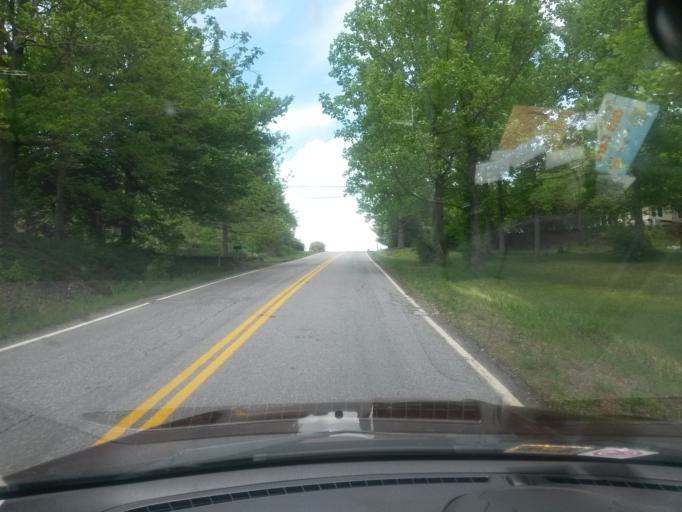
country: US
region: Virginia
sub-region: Floyd County
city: Floyd
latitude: 36.7575
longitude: -80.3916
